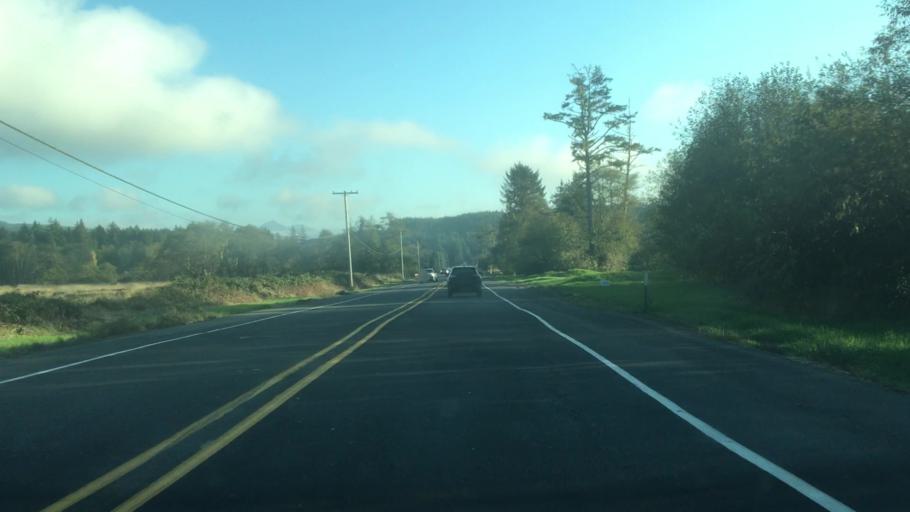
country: US
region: Oregon
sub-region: Clatsop County
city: Seaside
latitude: 45.9701
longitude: -123.9256
